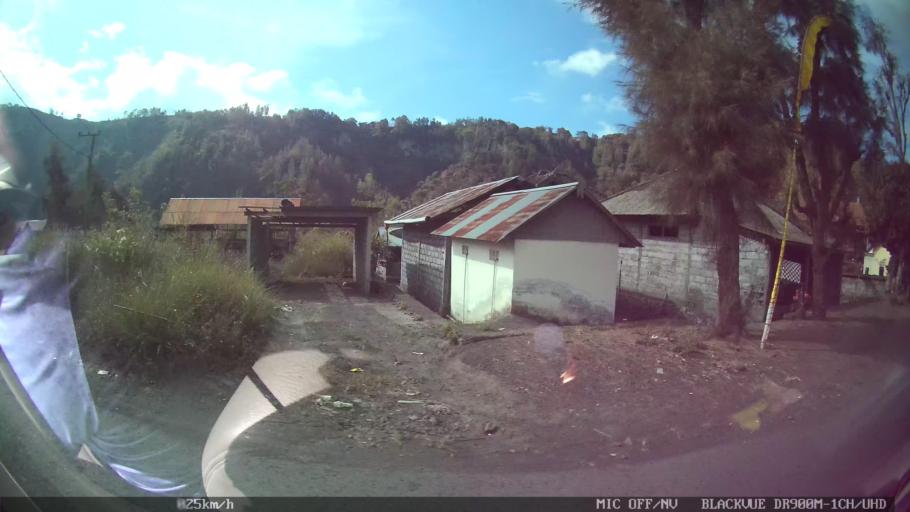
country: ID
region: Bali
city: Banjar Kedisan
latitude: -8.2159
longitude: 115.3716
